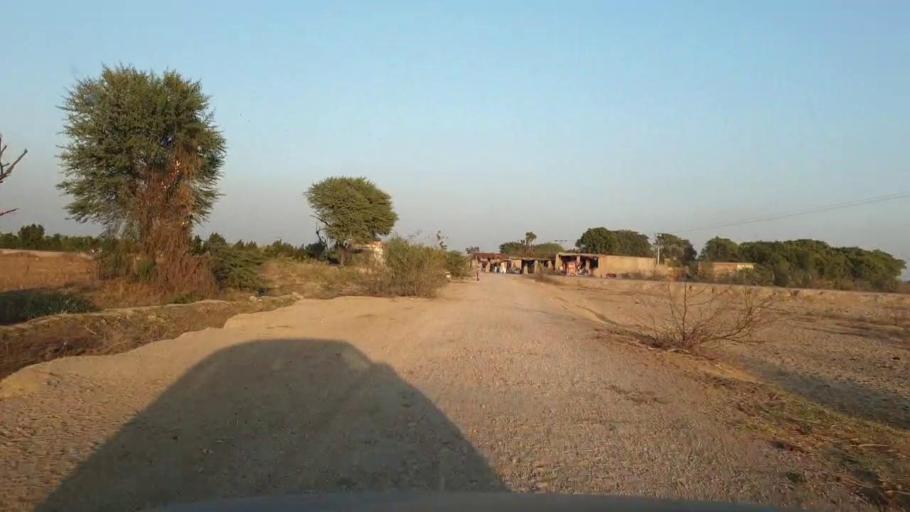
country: PK
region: Sindh
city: Chambar
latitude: 25.3162
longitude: 68.6599
